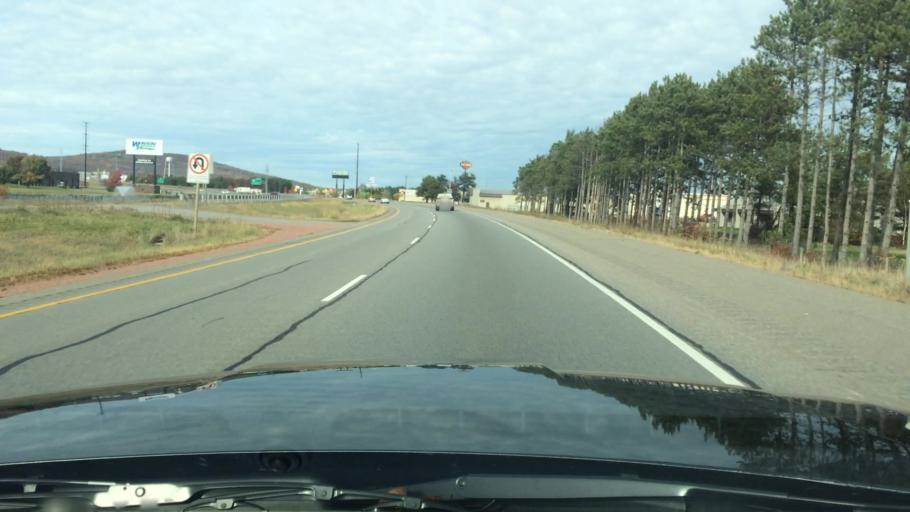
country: US
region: Wisconsin
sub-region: Marathon County
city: Evergreen
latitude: 44.8553
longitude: -89.6370
